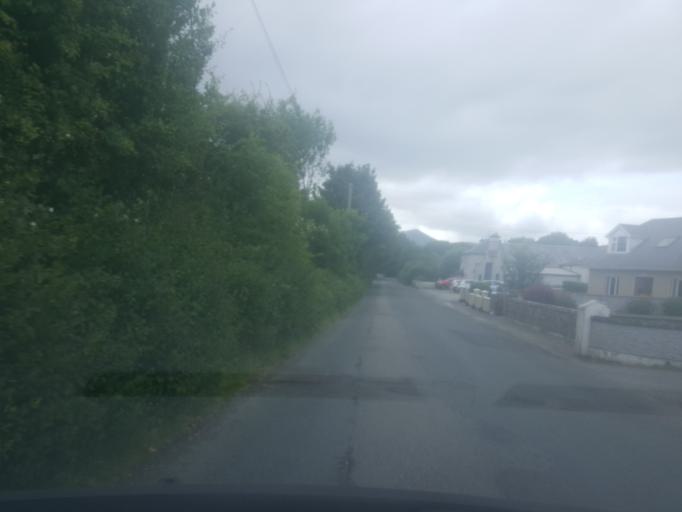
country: IE
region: Munster
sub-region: Ciarrai
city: Cill Airne
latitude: 52.0808
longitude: -9.4983
